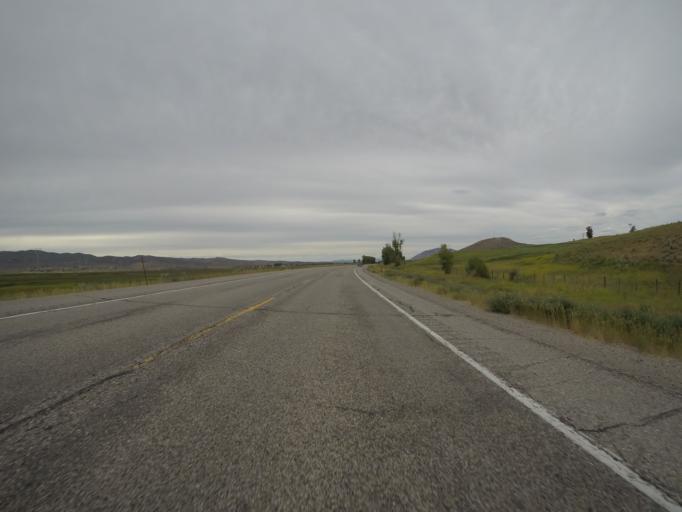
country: US
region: Idaho
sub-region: Bear Lake County
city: Montpelier
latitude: 42.0604
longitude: -110.9342
